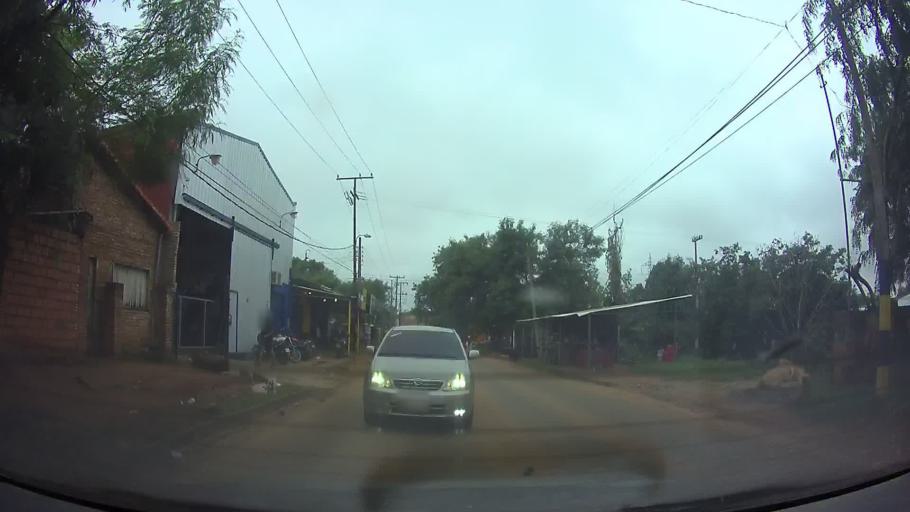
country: PY
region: Central
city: San Lorenzo
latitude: -25.3120
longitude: -57.4923
